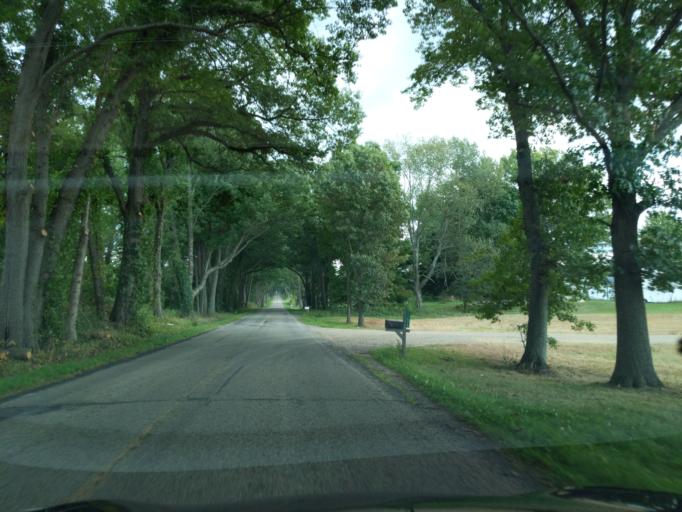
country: US
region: Michigan
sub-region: Eaton County
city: Eaton Rapids
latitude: 42.3785
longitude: -84.6113
